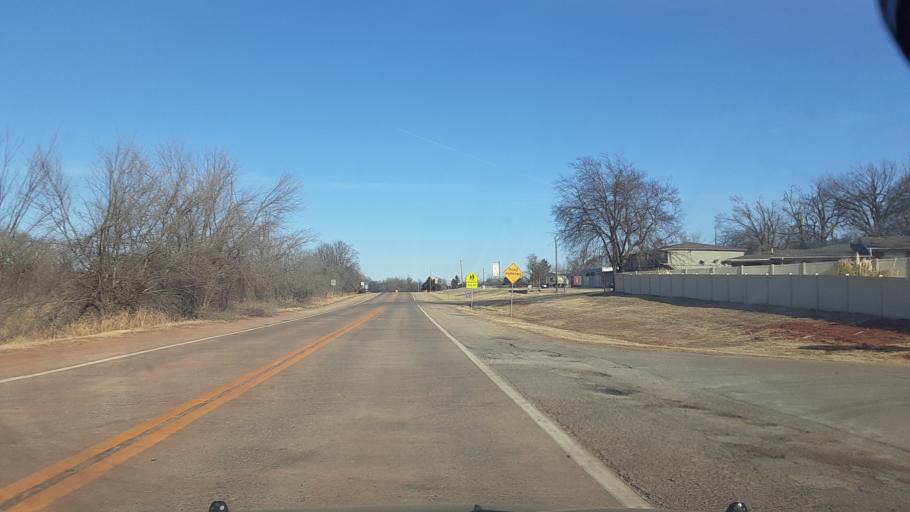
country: US
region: Oklahoma
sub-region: Logan County
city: Guthrie
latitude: 35.8901
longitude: -97.4240
